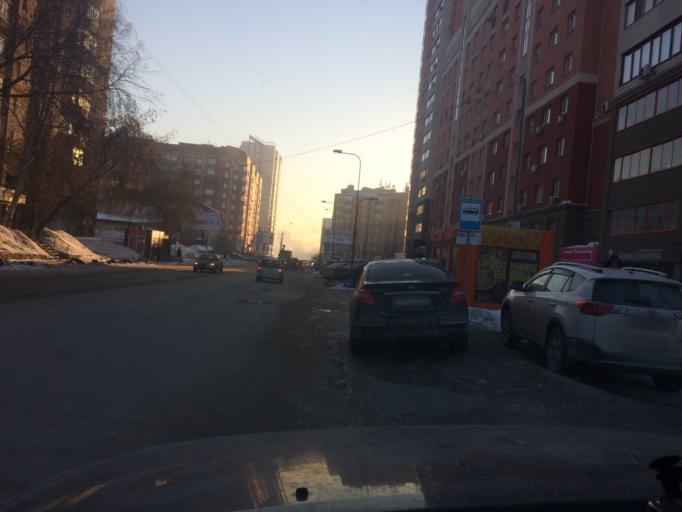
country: RU
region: Novosibirsk
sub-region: Novosibirskiy Rayon
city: Novosibirsk
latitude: 55.0319
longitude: 82.9299
